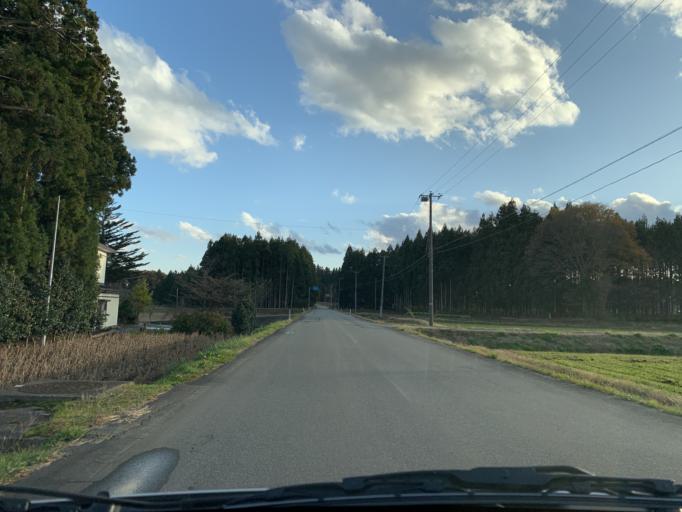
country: JP
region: Iwate
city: Mizusawa
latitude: 39.1215
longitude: 141.0367
